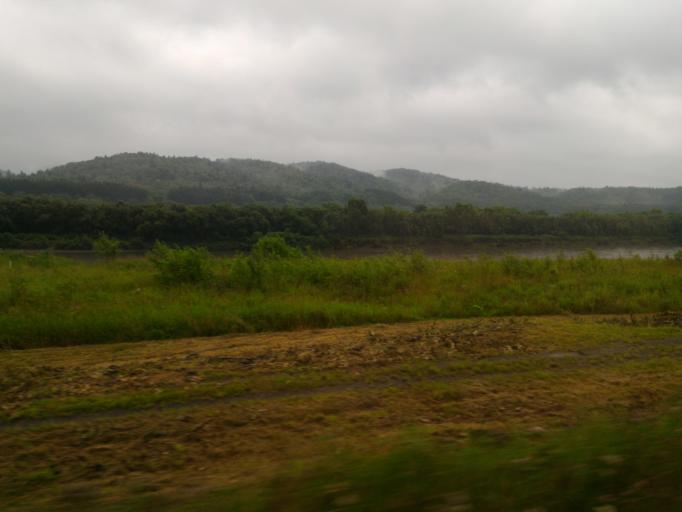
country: JP
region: Hokkaido
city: Nayoro
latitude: 44.7578
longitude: 142.0493
